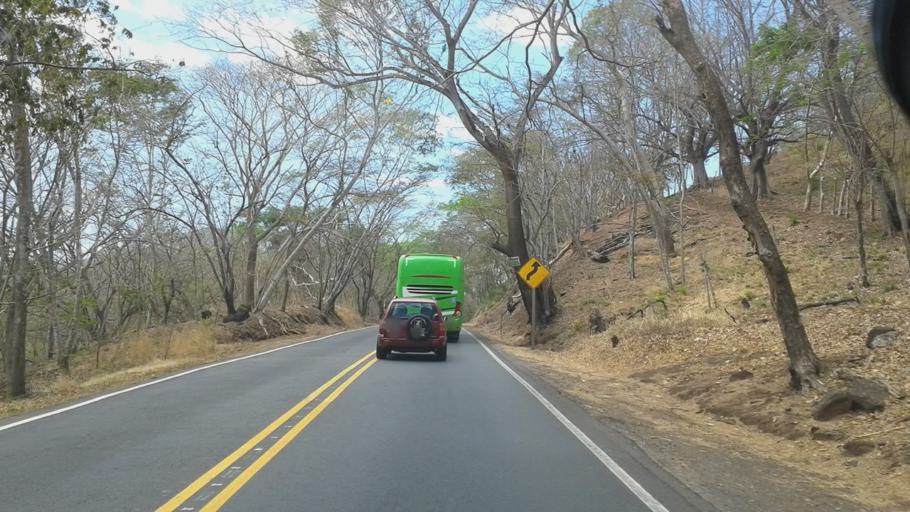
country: CR
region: Puntarenas
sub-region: Canton Central de Puntarenas
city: Puntarenas
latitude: 10.1188
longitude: -84.8970
